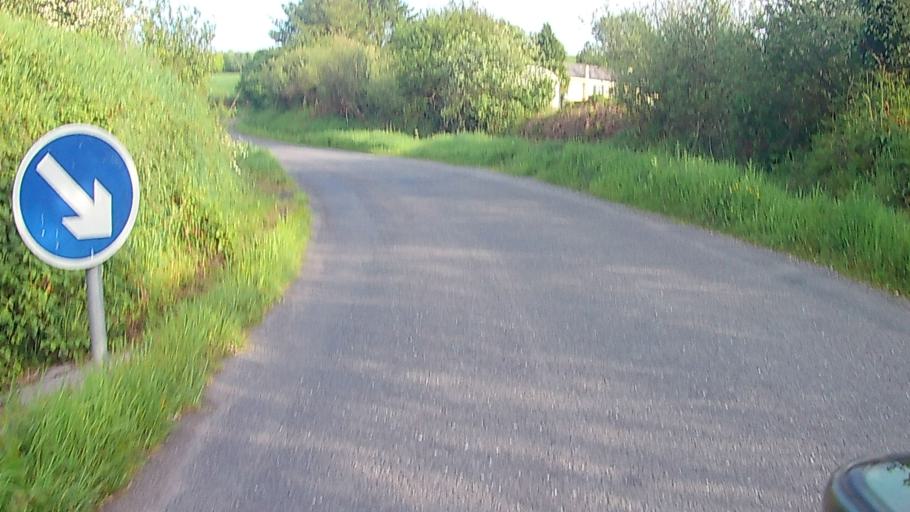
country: IE
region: Munster
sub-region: County Cork
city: Cork
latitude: 51.9743
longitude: -8.4627
